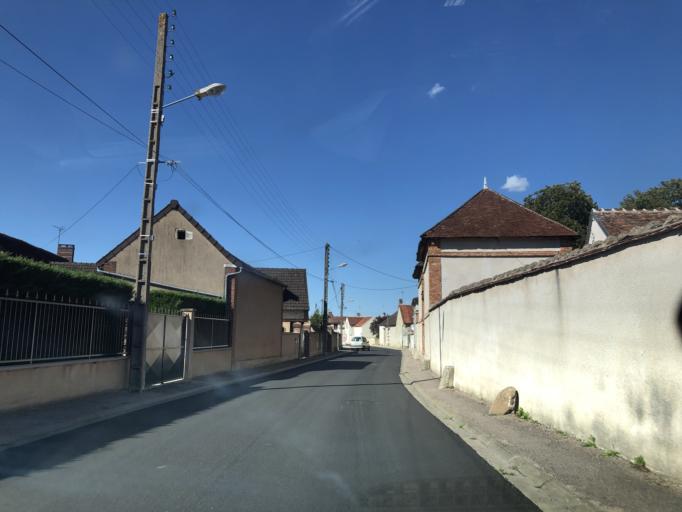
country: FR
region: Bourgogne
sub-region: Departement de l'Yonne
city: Appoigny
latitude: 47.8728
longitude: 3.5265
